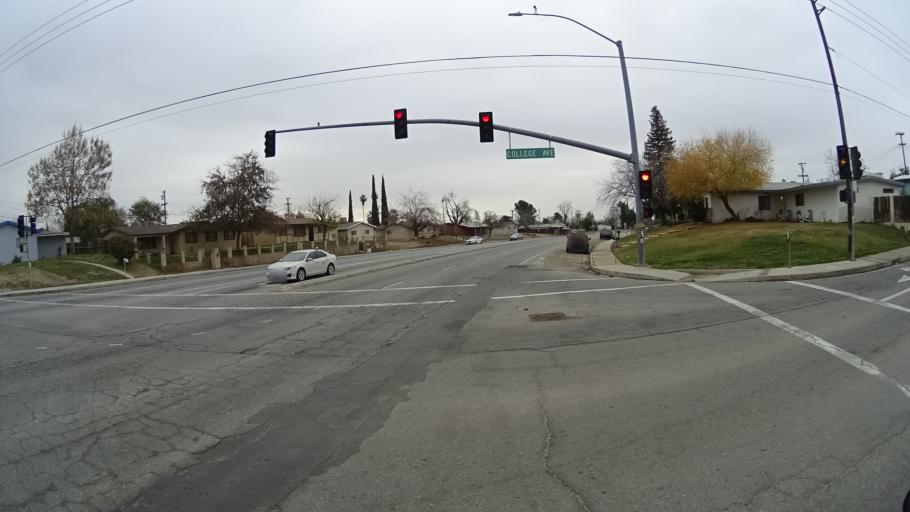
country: US
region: California
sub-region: Kern County
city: Bakersfield
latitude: 35.3834
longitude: -118.9304
